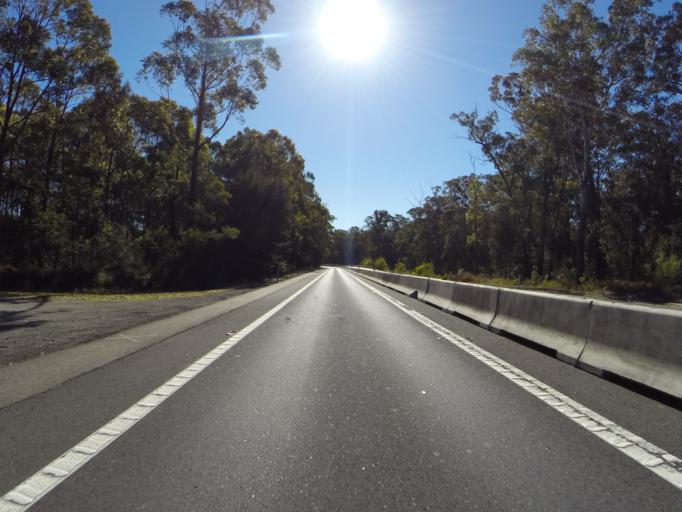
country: AU
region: New South Wales
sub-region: Wollondilly
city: Douglas Park
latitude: -34.2787
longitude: 150.7145
